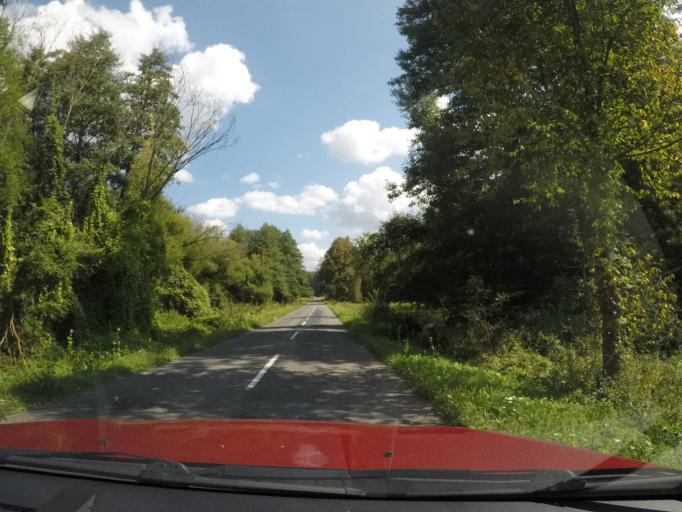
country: SK
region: Kosicky
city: Roznava
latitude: 48.6375
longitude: 20.6239
